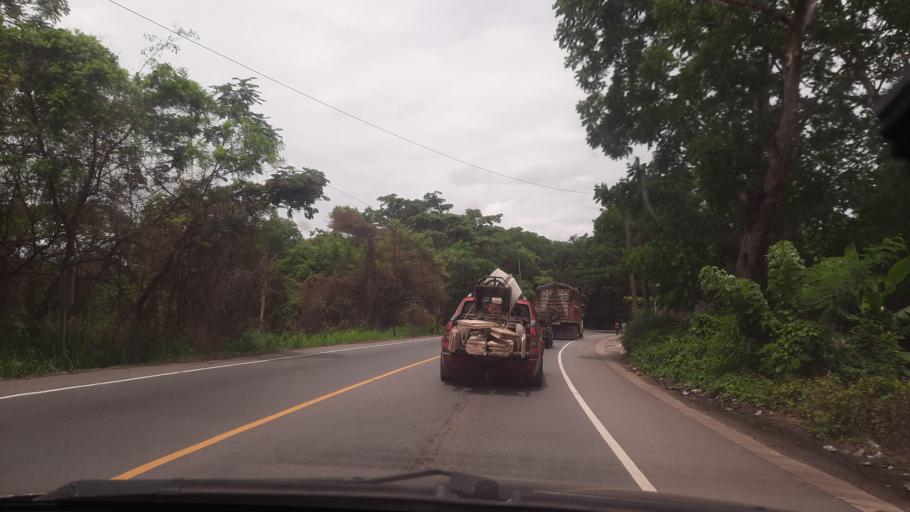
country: GT
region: Zacapa
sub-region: Municipio de Zacapa
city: Gualan
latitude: 15.2054
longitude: -89.2519
